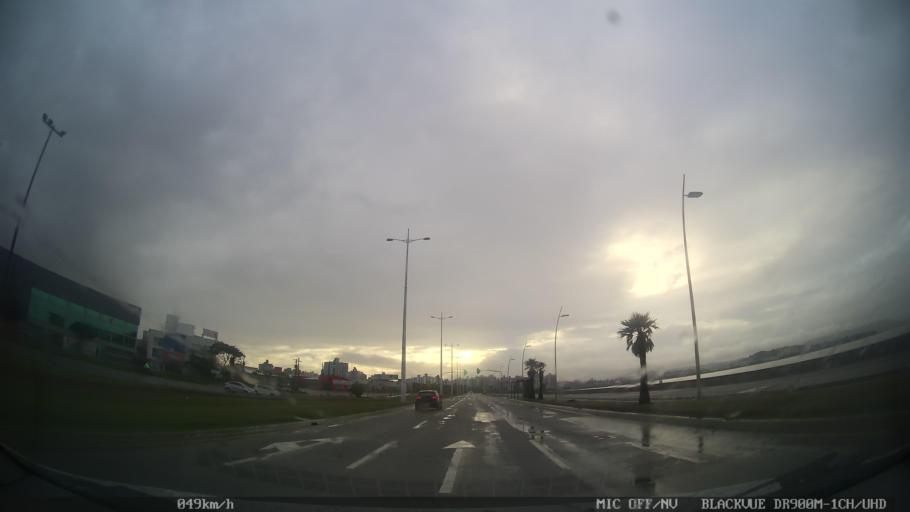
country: BR
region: Santa Catarina
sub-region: Sao Jose
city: Campinas
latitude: -27.6069
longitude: -48.6237
